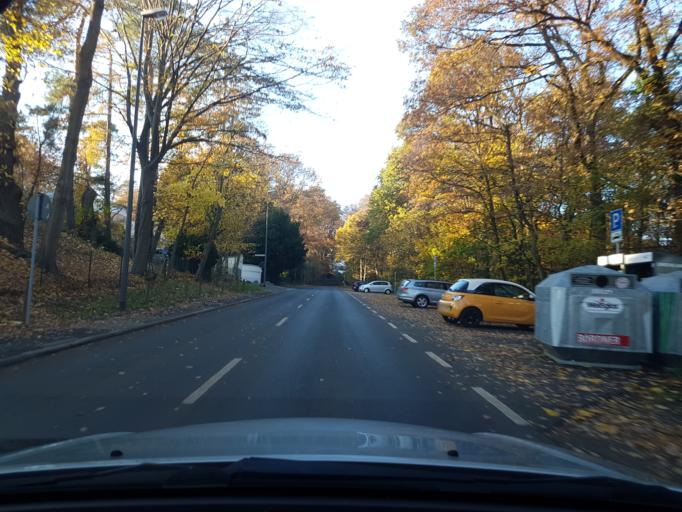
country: DE
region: Hesse
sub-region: Regierungsbezirk Darmstadt
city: Konigstein im Taunus
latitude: 50.1734
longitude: 8.4969
